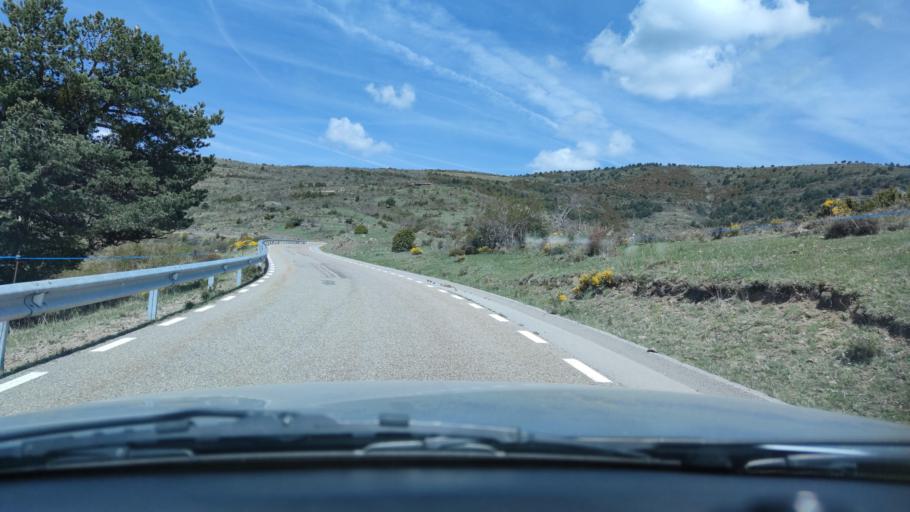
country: ES
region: Catalonia
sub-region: Provincia de Lleida
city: Coll de Nargo
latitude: 42.2940
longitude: 1.2385
